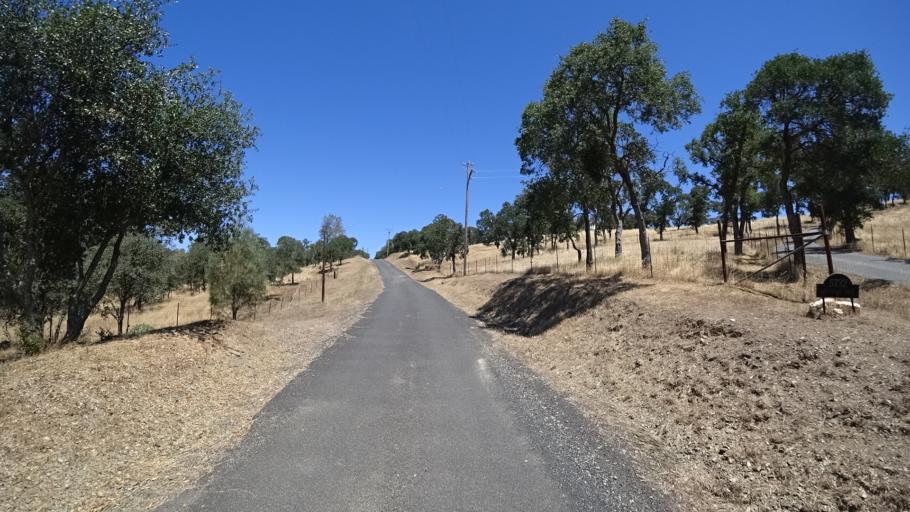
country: US
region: California
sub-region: Calaveras County
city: Copperopolis
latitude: 37.9912
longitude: -120.7007
